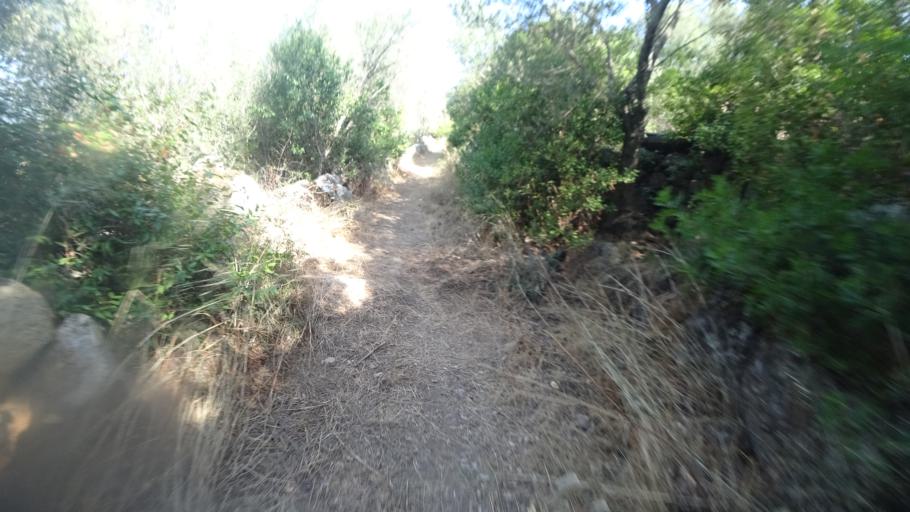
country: FR
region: Corsica
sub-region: Departement de la Corse-du-Sud
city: Porto-Vecchio
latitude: 41.6629
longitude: 9.3275
